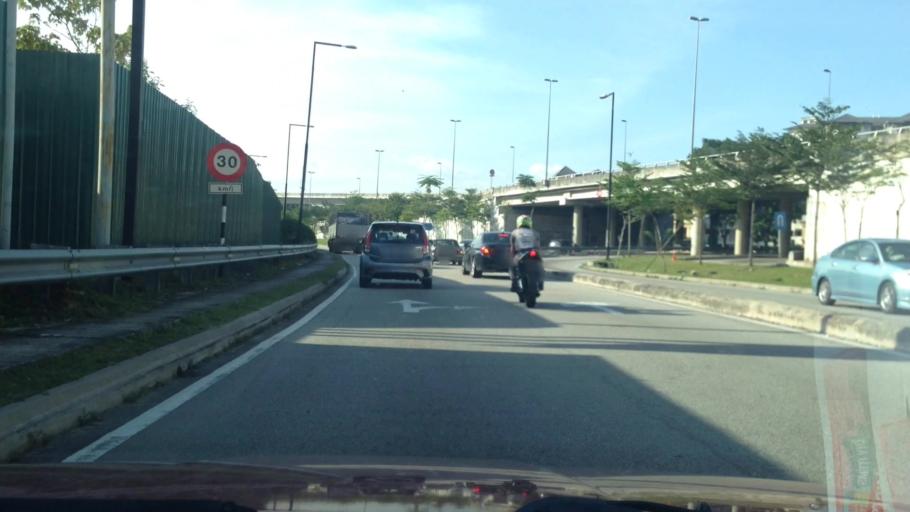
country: MY
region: Selangor
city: Subang Jaya
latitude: 3.0273
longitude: 101.5799
